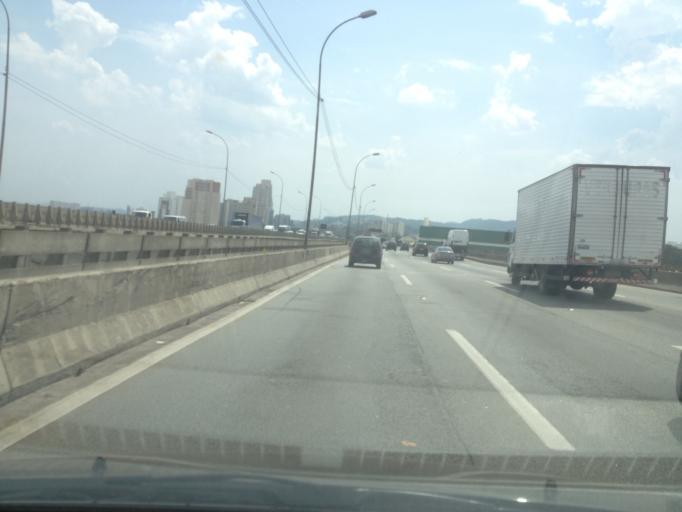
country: BR
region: Sao Paulo
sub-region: Barueri
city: Barueri
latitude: -23.5049
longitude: -46.8583
